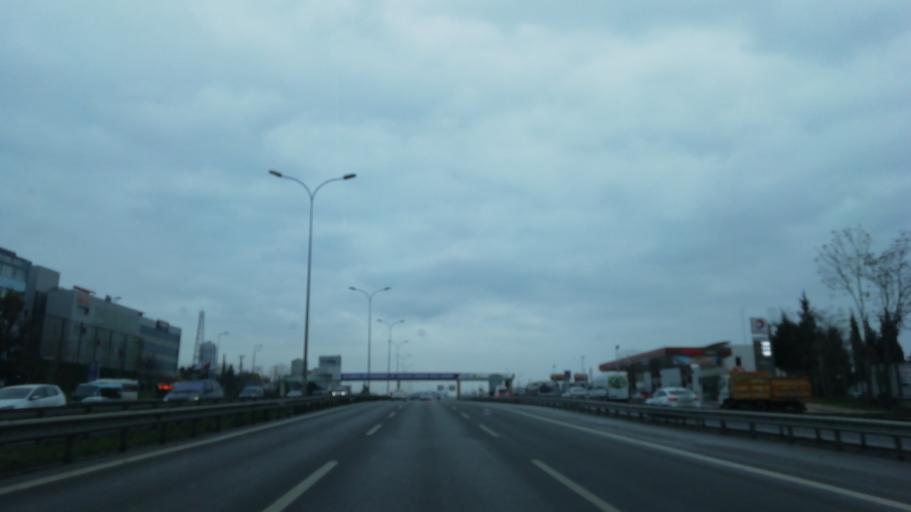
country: TR
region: Istanbul
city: Maltepe
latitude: 40.9095
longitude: 29.2018
